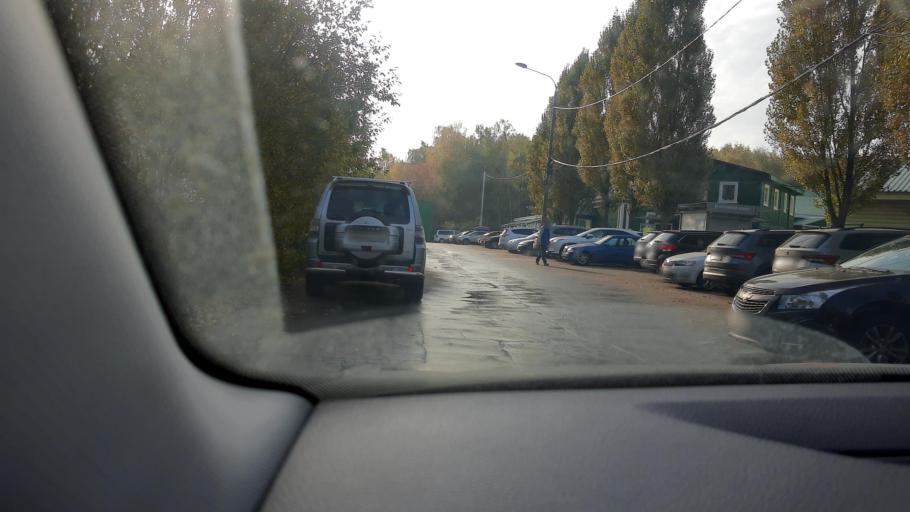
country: RU
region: Moscow
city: Annino
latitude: 55.5612
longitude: 37.5720
